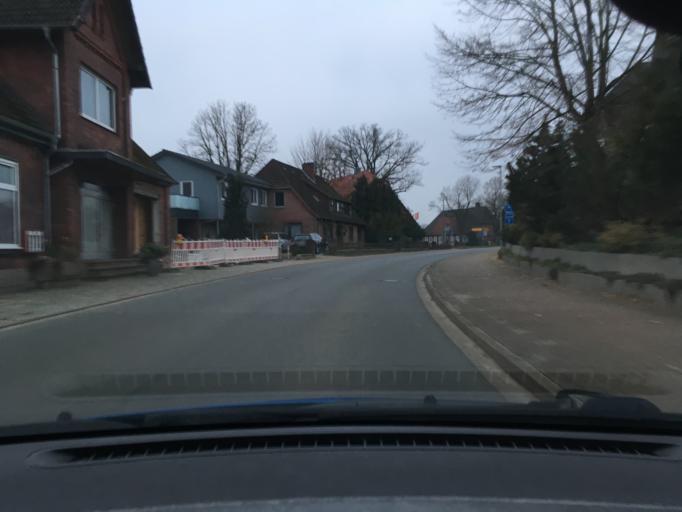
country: DE
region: Lower Saxony
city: Bispingen
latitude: 53.1118
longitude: 9.9608
